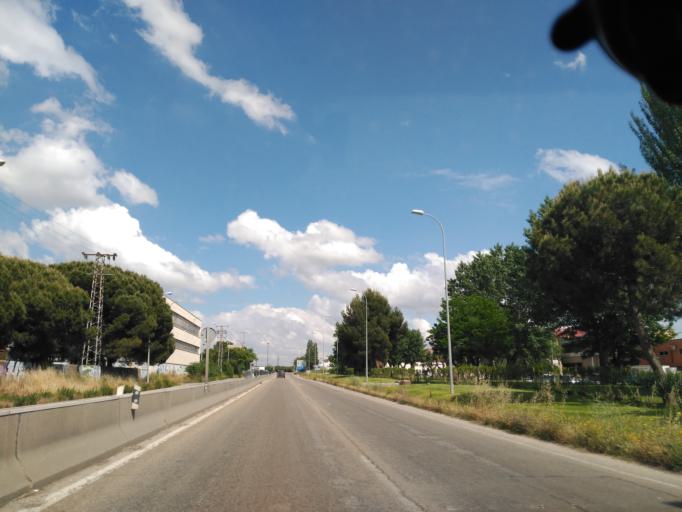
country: ES
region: Madrid
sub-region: Provincia de Madrid
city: Getafe
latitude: 40.3038
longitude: -3.6984
